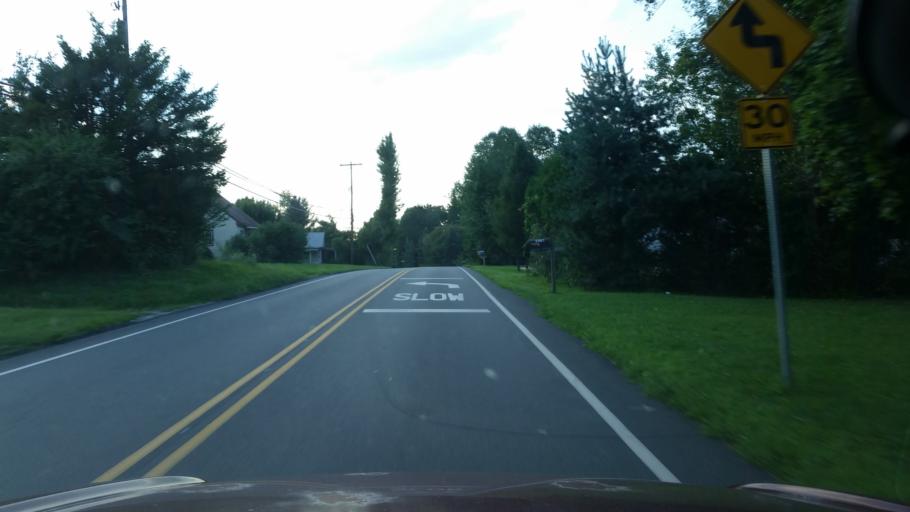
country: US
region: Pennsylvania
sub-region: Lebanon County
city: Campbelltown
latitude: 40.2612
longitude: -76.5548
